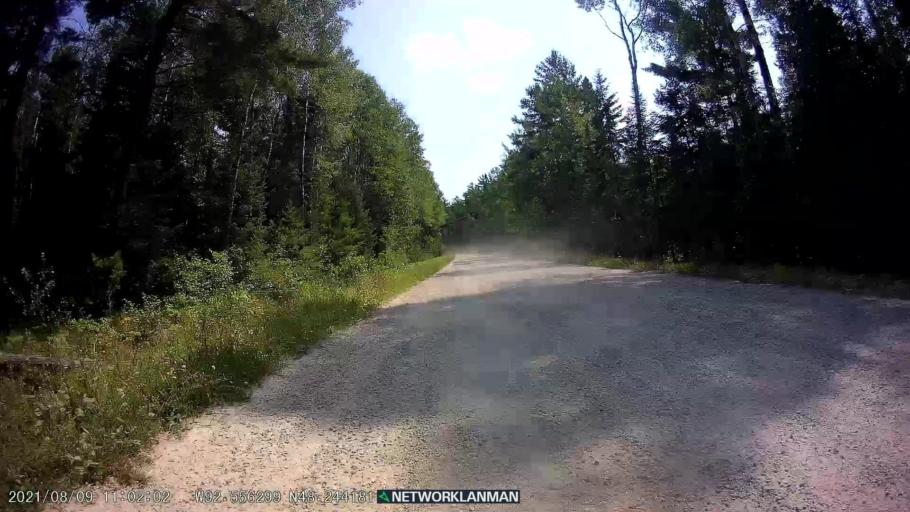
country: US
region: Minnesota
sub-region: Saint Louis County
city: Parkville
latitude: 48.2442
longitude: -92.5564
